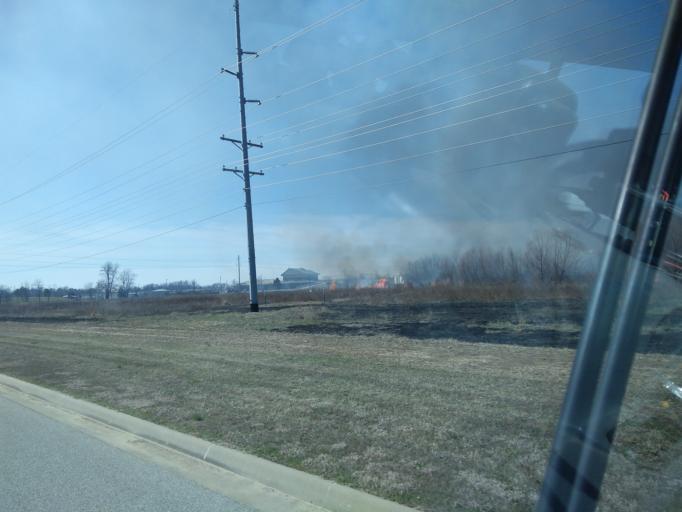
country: US
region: Arkansas
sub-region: Washington County
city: Farmington
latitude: 36.0667
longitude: -94.2311
